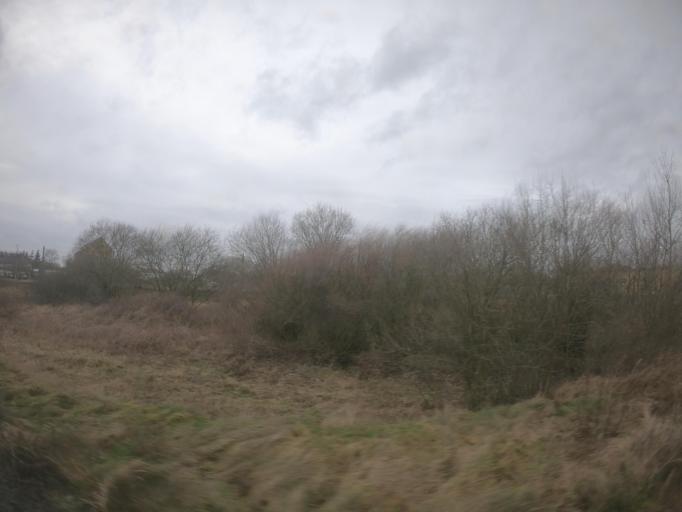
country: PL
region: West Pomeranian Voivodeship
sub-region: Powiat szczecinecki
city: Szczecinek
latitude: 53.7017
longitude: 16.7187
